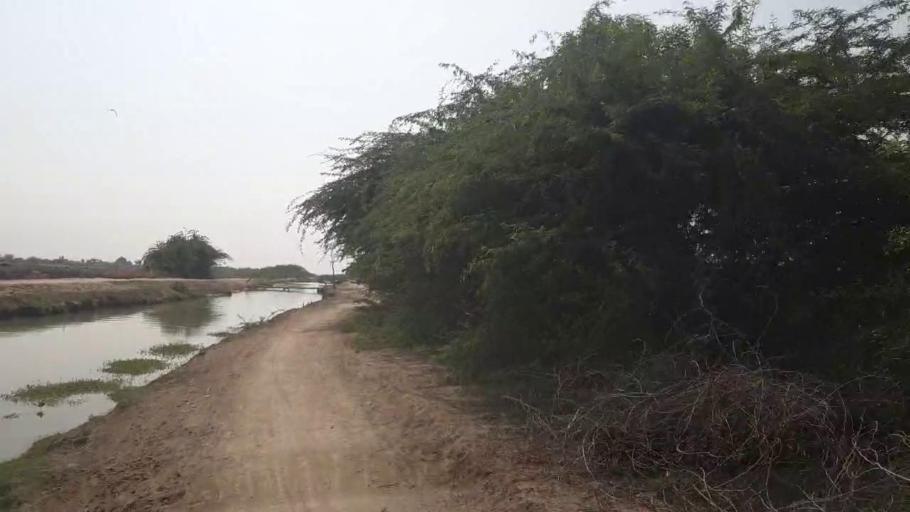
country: PK
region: Sindh
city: Kadhan
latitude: 24.5067
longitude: 68.8502
